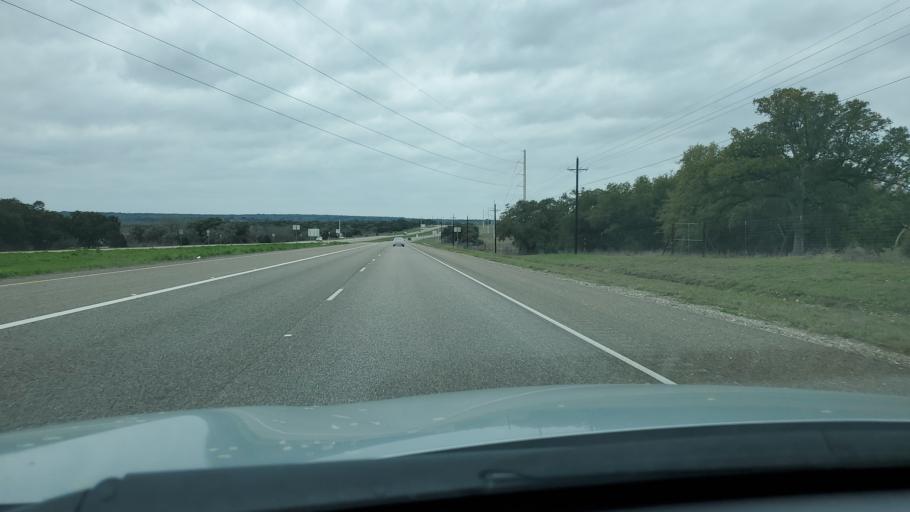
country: US
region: Texas
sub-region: Williamson County
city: Serenada
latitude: 30.7594
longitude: -97.7296
